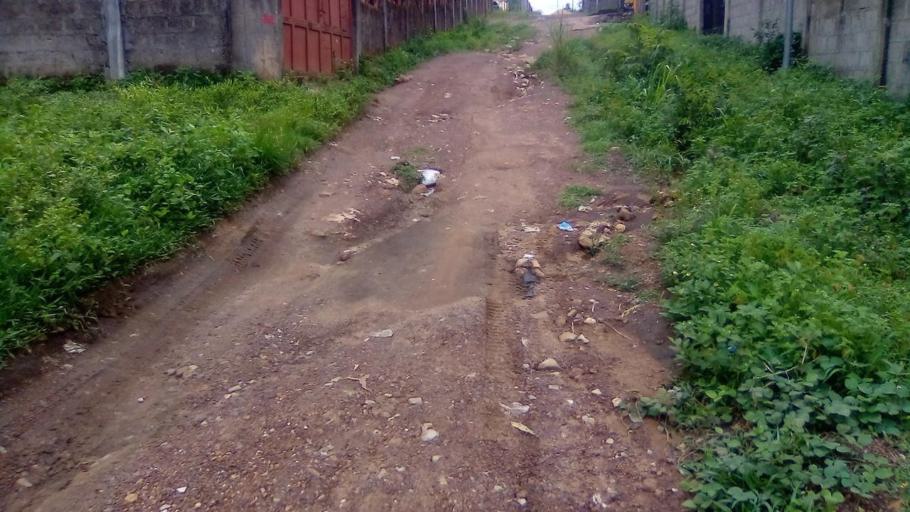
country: SL
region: Southern Province
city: Bo
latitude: 7.9444
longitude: -11.7413
